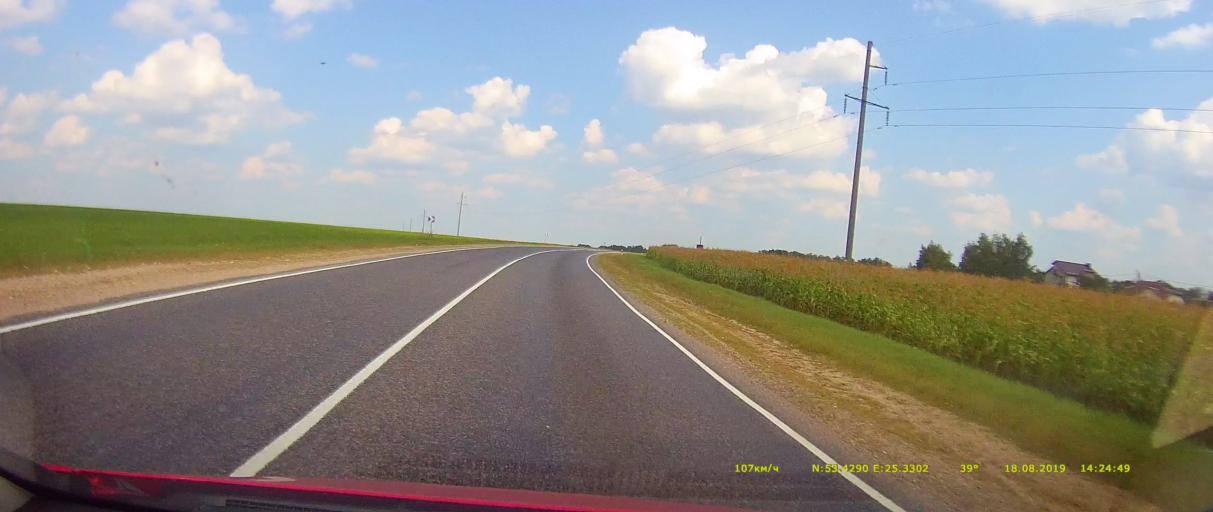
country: BY
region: Grodnenskaya
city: Dzyatlava
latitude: 53.4427
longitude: 25.3554
